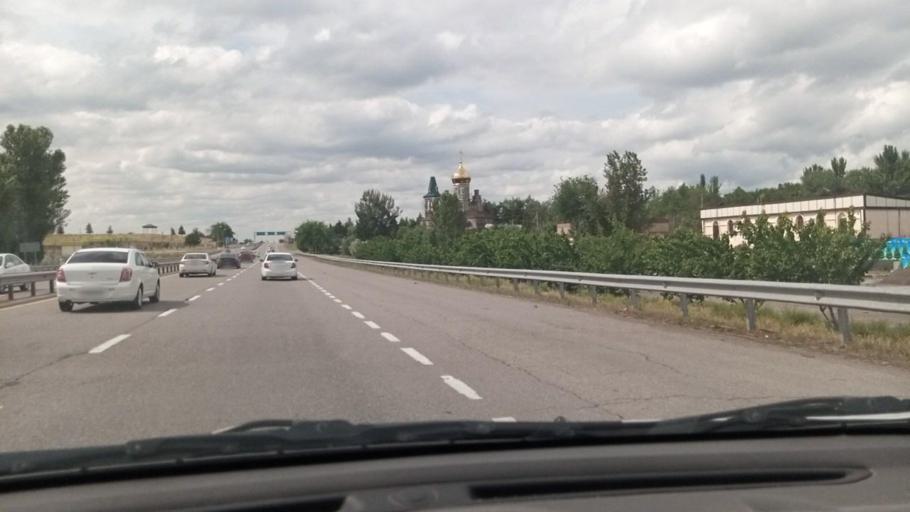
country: UZ
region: Toshkent
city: Tuytepa
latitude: 41.1180
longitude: 69.4437
